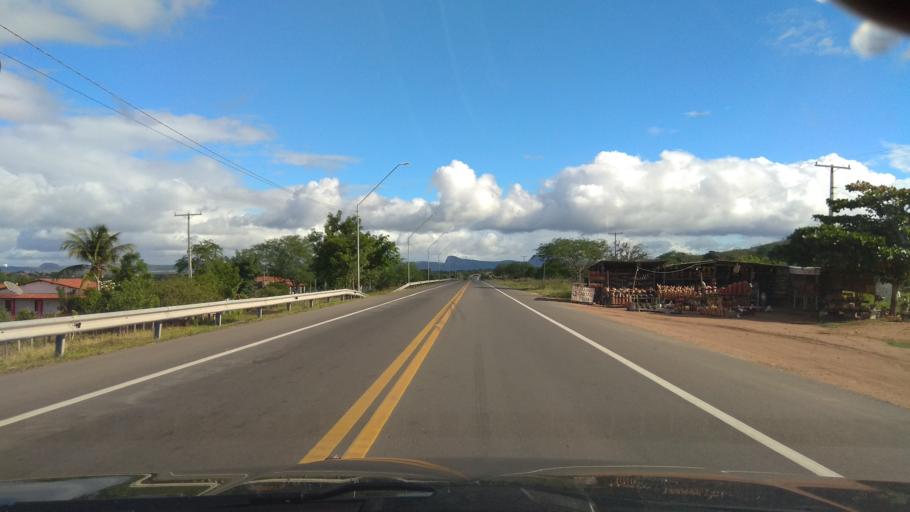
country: BR
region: Bahia
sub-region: Castro Alves
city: Castro Alves
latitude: -12.6392
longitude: -39.6015
